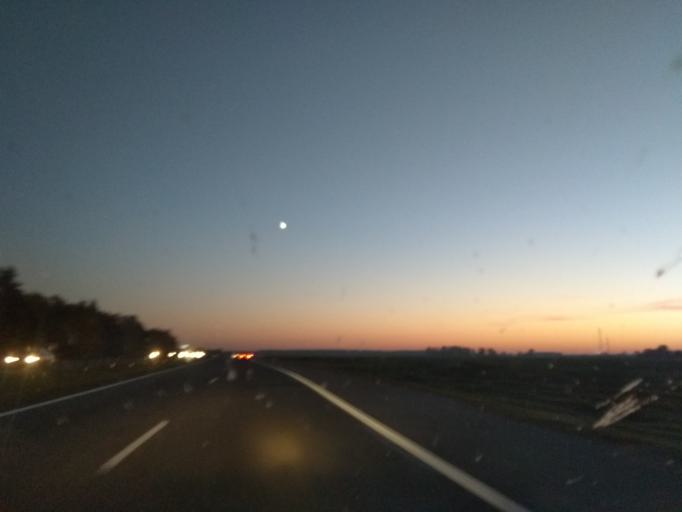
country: BY
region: Minsk
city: Enyerhyetykaw
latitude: 53.6192
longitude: 27.0518
